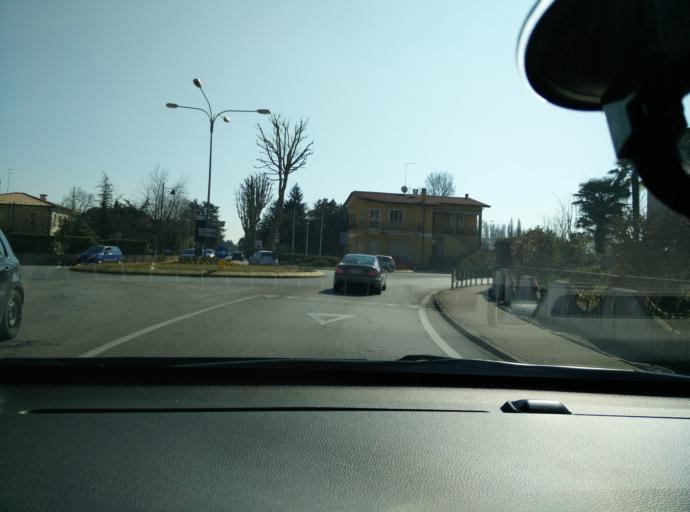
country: IT
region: Veneto
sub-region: Provincia di Venezia
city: San Dona di Piave
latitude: 45.6410
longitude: 12.5547
